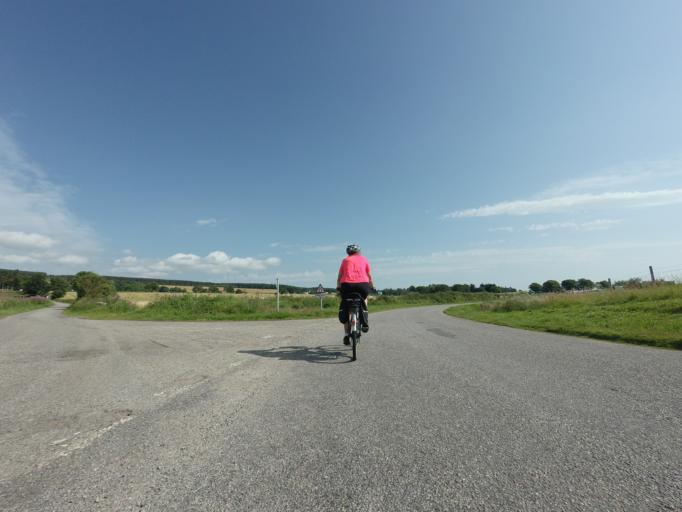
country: GB
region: Scotland
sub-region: Highland
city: Alness
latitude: 57.7100
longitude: -4.2267
